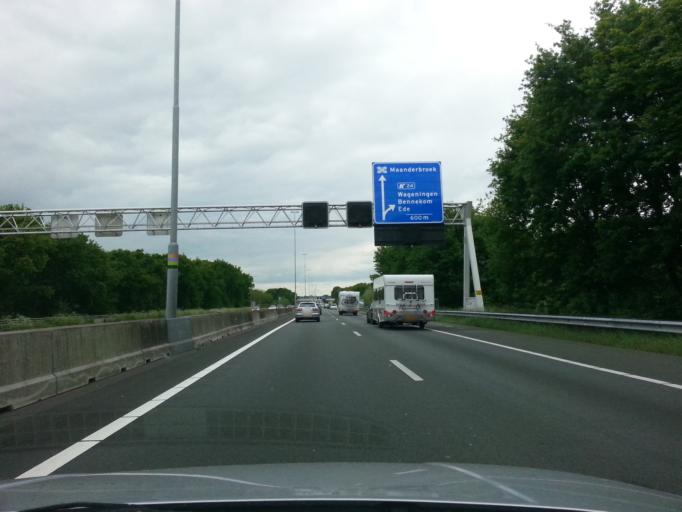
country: NL
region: Gelderland
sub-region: Gemeente Ede
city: Bennekom
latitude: 52.0130
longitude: 5.6695
